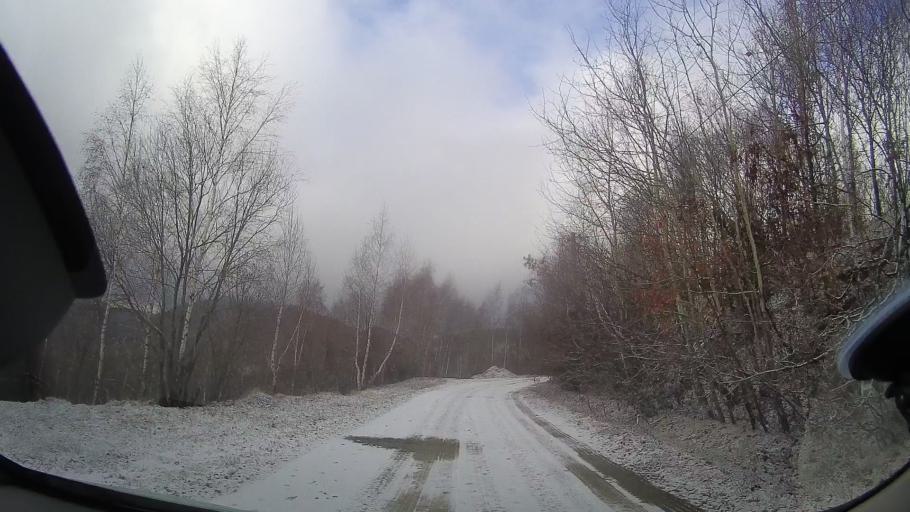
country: RO
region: Cluj
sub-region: Comuna Valea Ierii
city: Valea Ierii
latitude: 46.6547
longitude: 23.3503
